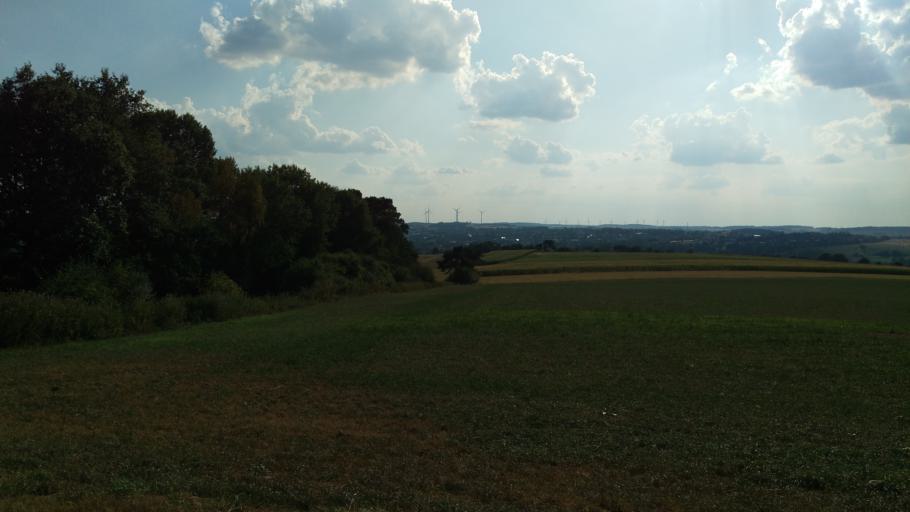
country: DE
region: Hesse
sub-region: Regierungsbezirk Giessen
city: Alsfeld
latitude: 50.7633
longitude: 9.3120
